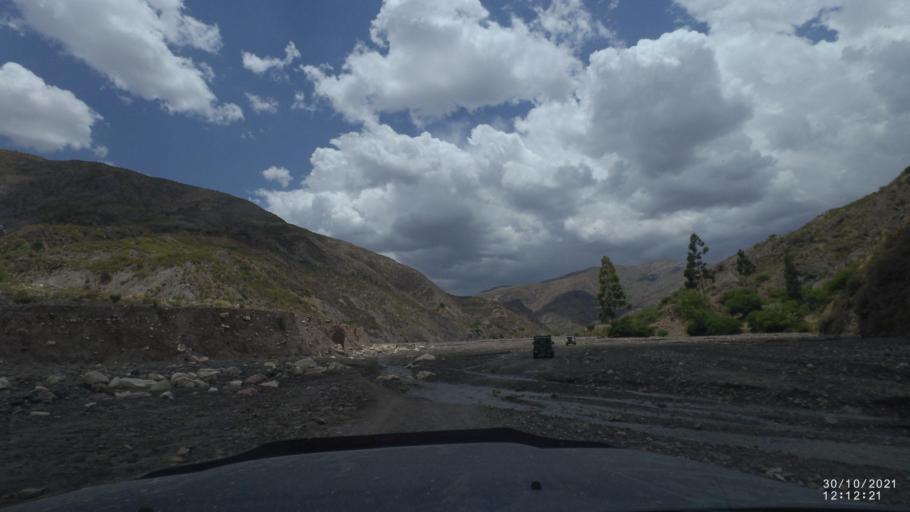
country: BO
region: Cochabamba
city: Colchani
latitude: -17.5536
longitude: -66.6238
